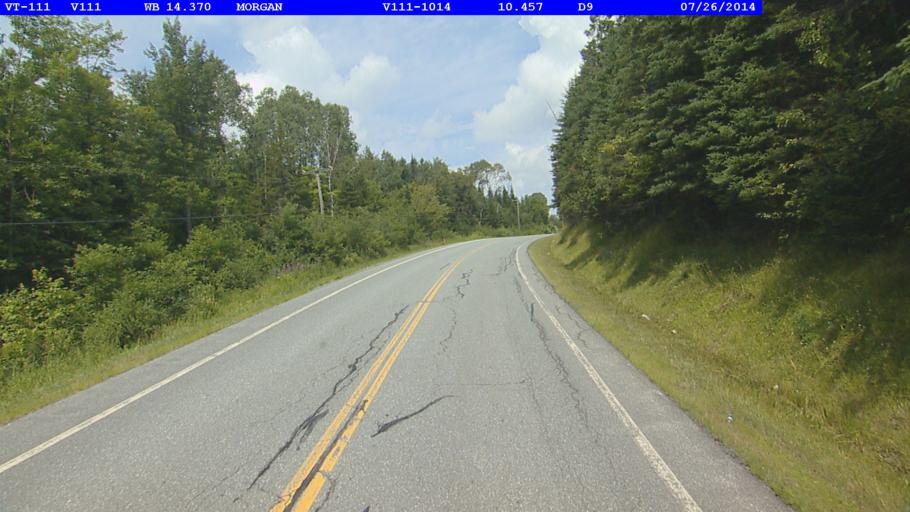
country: US
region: Vermont
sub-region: Orleans County
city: Newport
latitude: 44.8536
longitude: -71.9177
